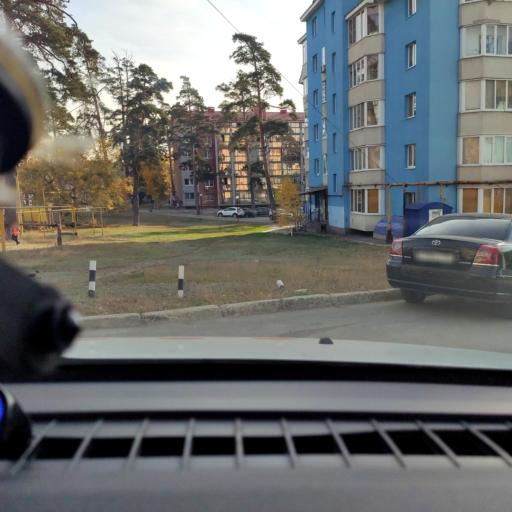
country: RU
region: Samara
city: Volzhskiy
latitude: 53.4365
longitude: 50.1256
